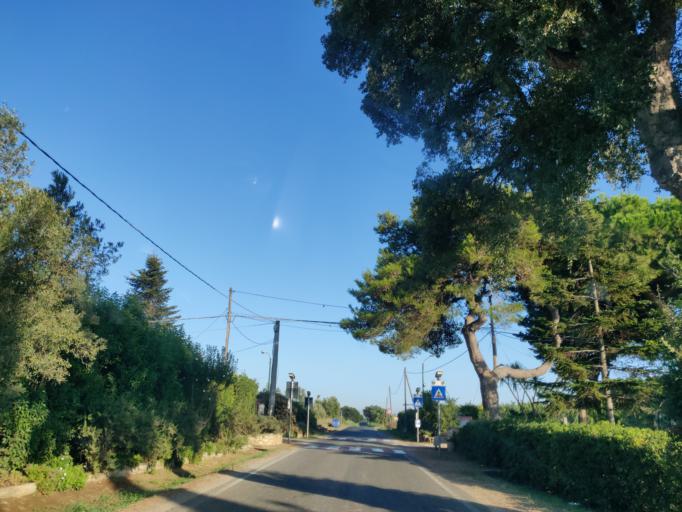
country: IT
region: Latium
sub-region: Provincia di Viterbo
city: Montalto di Castro
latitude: 42.2957
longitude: 11.6500
